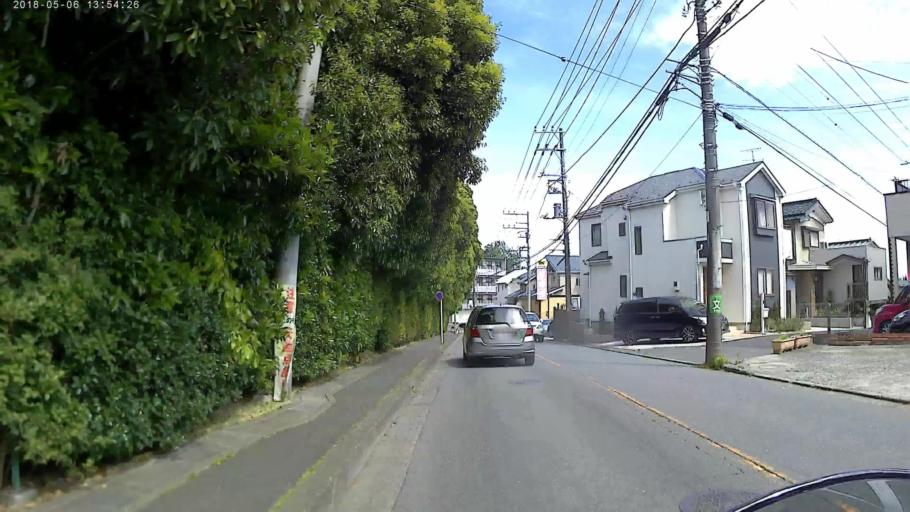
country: JP
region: Kanagawa
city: Yokohama
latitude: 35.4337
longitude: 139.5791
